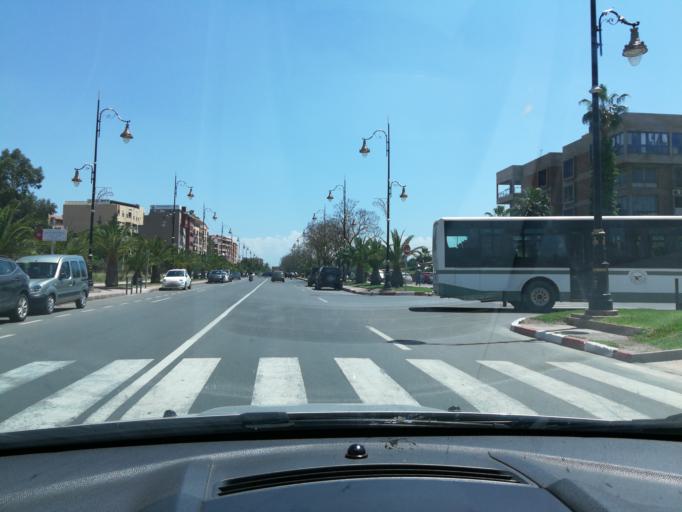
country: MA
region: Marrakech-Tensift-Al Haouz
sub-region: Marrakech
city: Marrakesh
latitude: 31.6382
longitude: -8.0214
